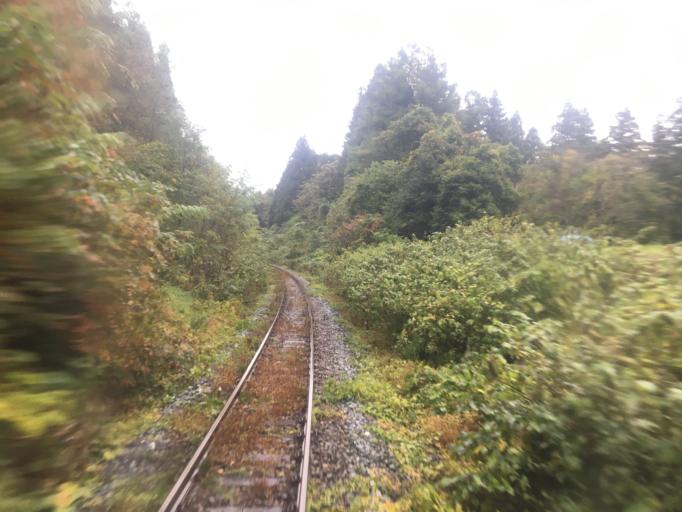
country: JP
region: Yamagata
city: Shinjo
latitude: 38.7105
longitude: 140.3687
